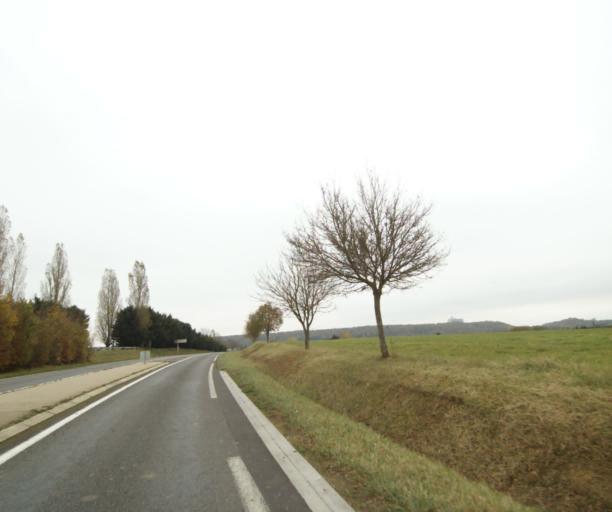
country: FR
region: Lorraine
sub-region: Departement de Meurthe-et-Moselle
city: Mancieulles
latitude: 49.2731
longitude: 5.9125
